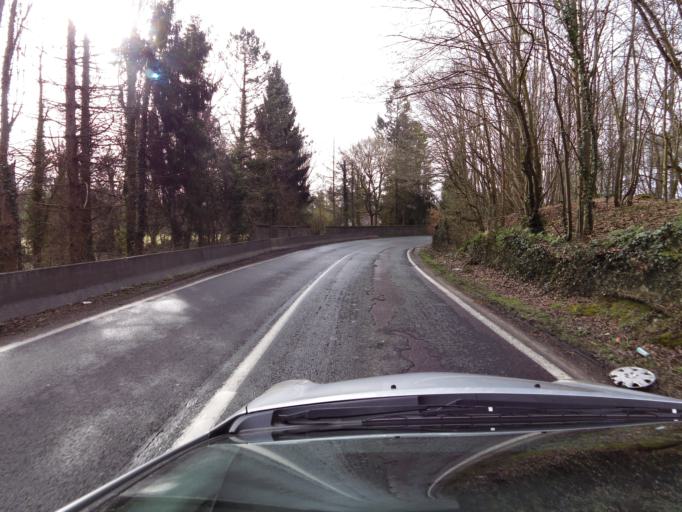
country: FR
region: Picardie
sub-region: Departement de l'Oise
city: Ver-sur-Launette
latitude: 49.1336
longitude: 2.6915
